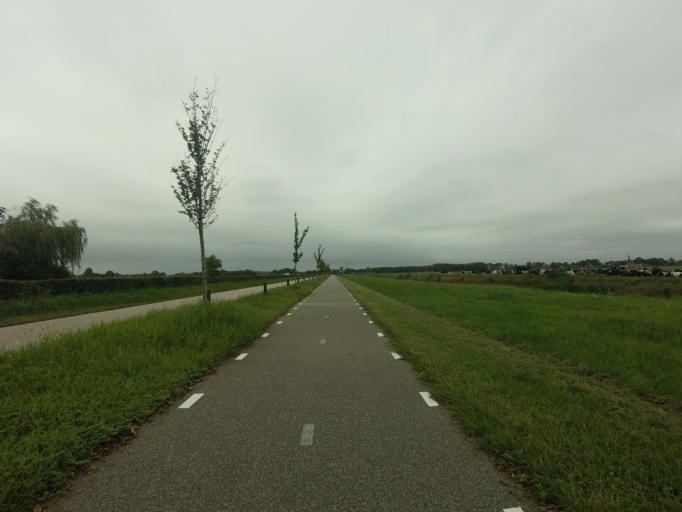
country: NL
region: Friesland
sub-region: Gemeente Opsterland
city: Gorredijk
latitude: 53.0109
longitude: 6.0356
